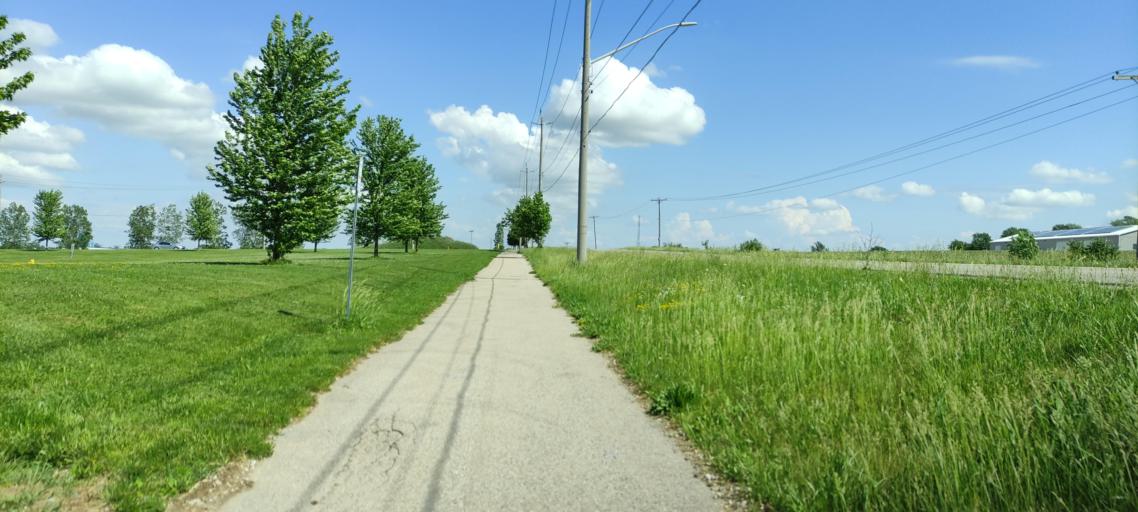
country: CA
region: Ontario
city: Stratford
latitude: 43.3428
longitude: -81.0148
